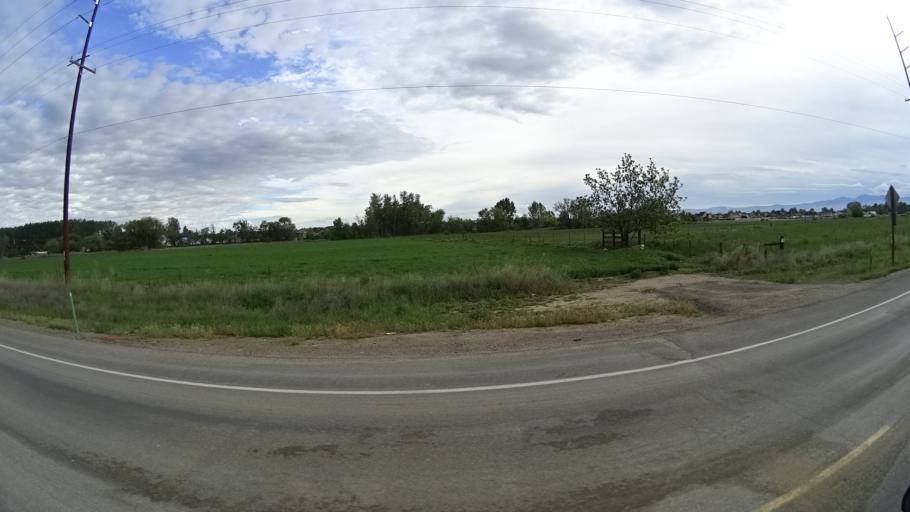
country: US
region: Idaho
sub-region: Ada County
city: Star
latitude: 43.6933
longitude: -116.5108
